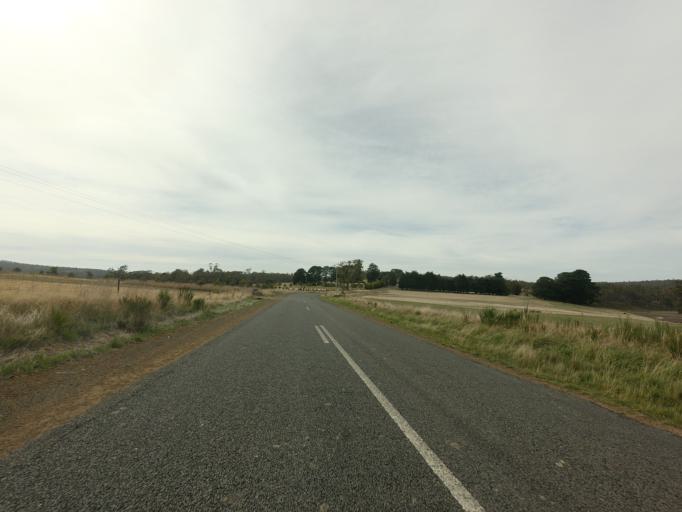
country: AU
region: Tasmania
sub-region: Brighton
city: Bridgewater
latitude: -42.3900
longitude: 147.4274
